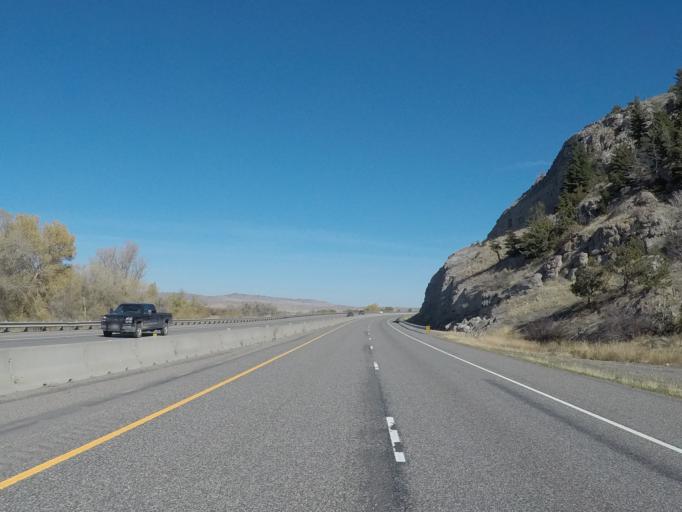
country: US
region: Montana
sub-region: Sweet Grass County
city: Big Timber
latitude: 45.7298
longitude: -110.2361
